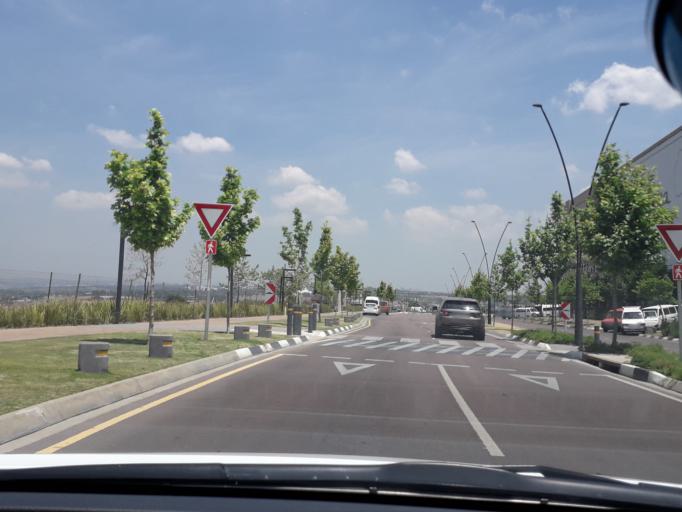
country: ZA
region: Gauteng
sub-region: City of Johannesburg Metropolitan Municipality
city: Midrand
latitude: -26.0157
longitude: 28.1097
